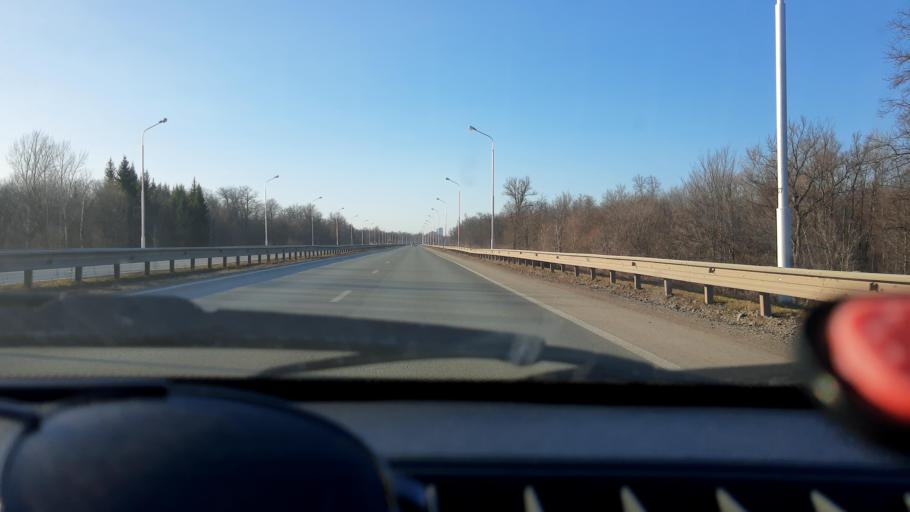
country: RU
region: Bashkortostan
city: Ufa
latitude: 54.6713
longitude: 56.0379
